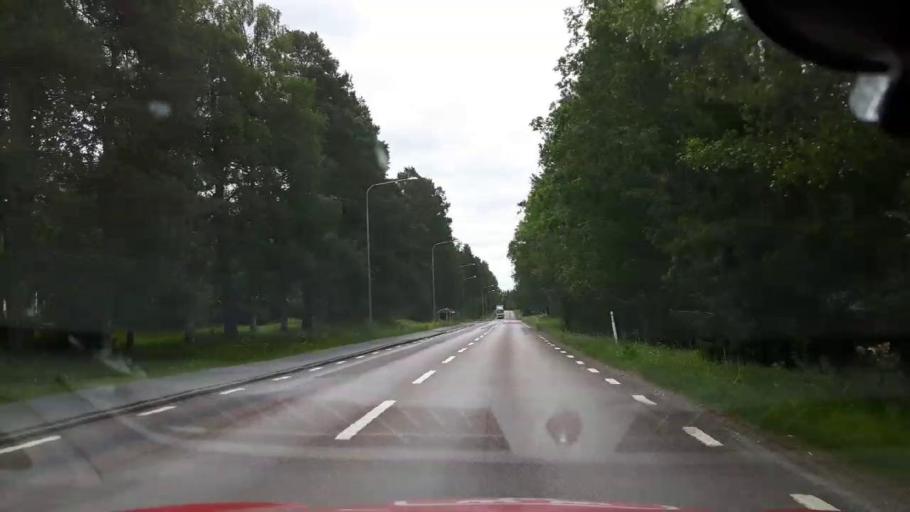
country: SE
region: Jaemtland
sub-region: OEstersunds Kommun
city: Brunflo
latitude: 62.9542
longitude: 15.0459
